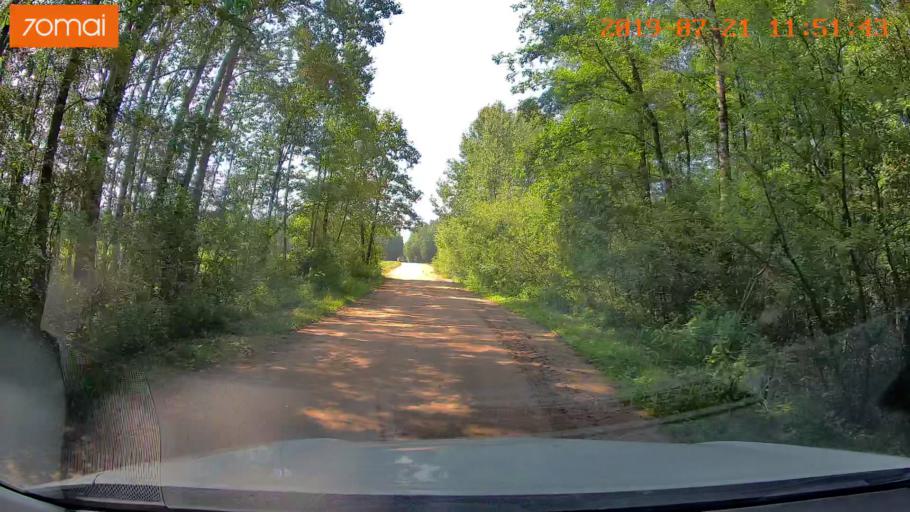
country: BY
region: Grodnenskaya
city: Lyubcha
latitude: 53.8820
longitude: 26.0109
